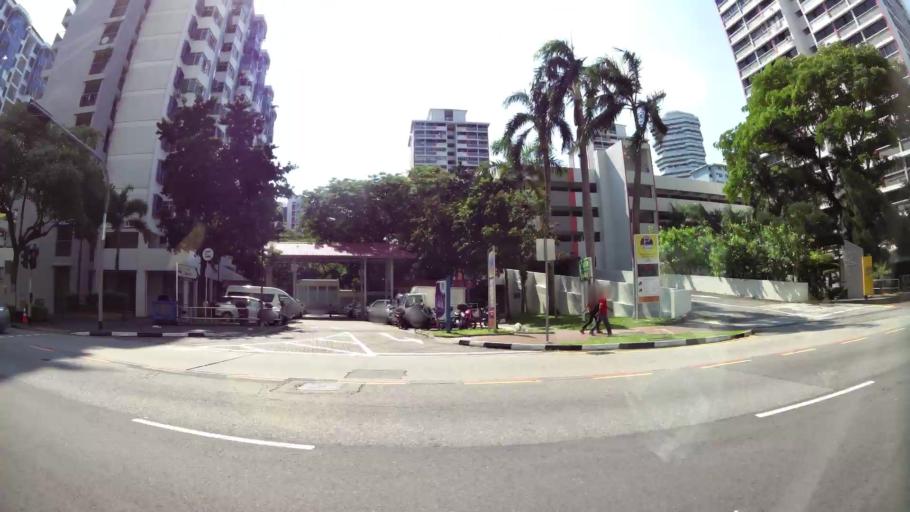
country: SG
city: Singapore
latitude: 1.3047
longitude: 103.8631
